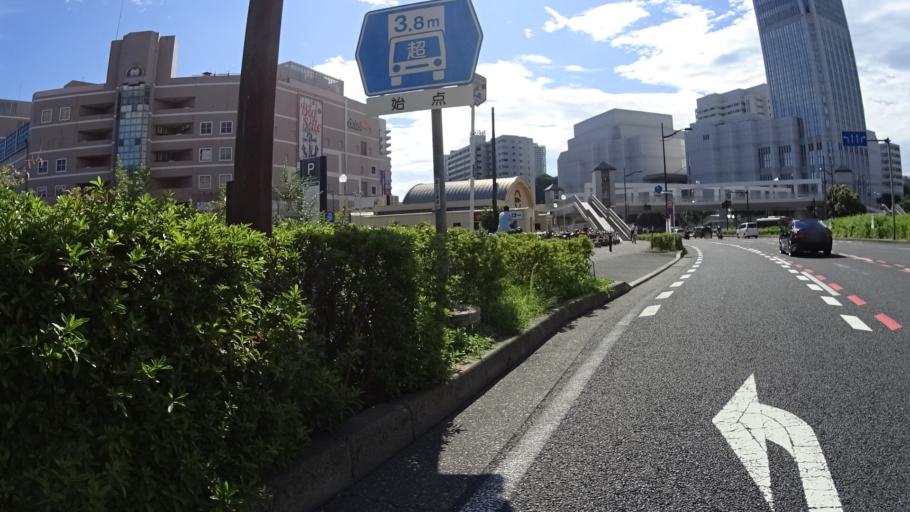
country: JP
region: Kanagawa
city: Yokosuka
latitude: 35.2820
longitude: 139.6608
